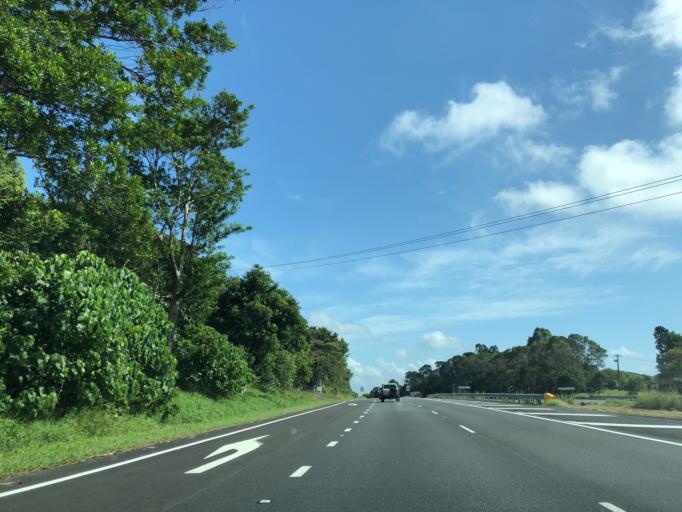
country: AU
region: New South Wales
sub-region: Byron Shire
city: Byron Bay
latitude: -28.6273
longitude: 153.5489
